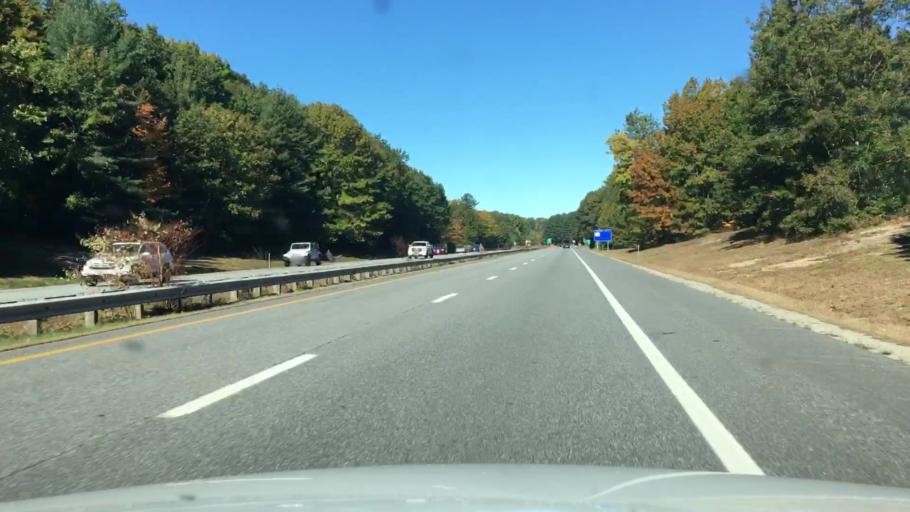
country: US
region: New Hampshire
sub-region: Strafford County
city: Dover
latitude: 43.1675
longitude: -70.8582
